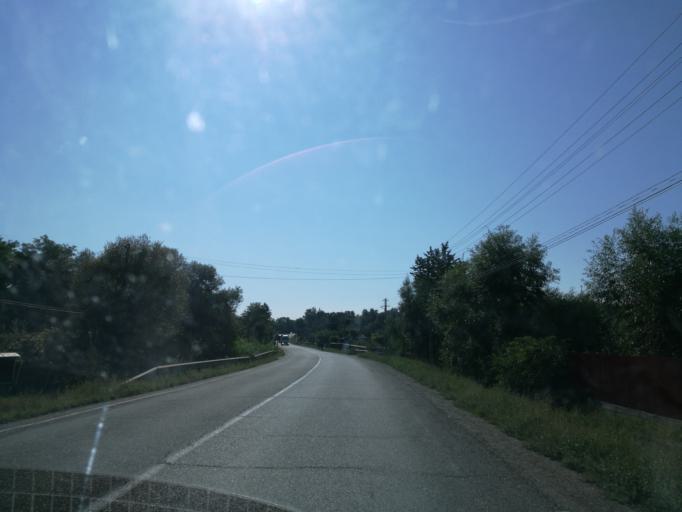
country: RO
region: Suceava
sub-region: Comuna Draguseni
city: Draguseni
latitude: 47.3066
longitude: 26.4792
